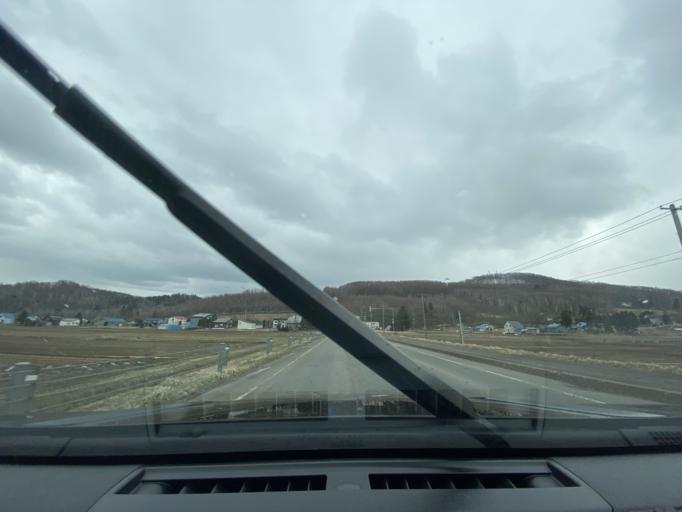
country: JP
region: Hokkaido
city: Nayoro
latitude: 44.1698
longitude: 142.2689
